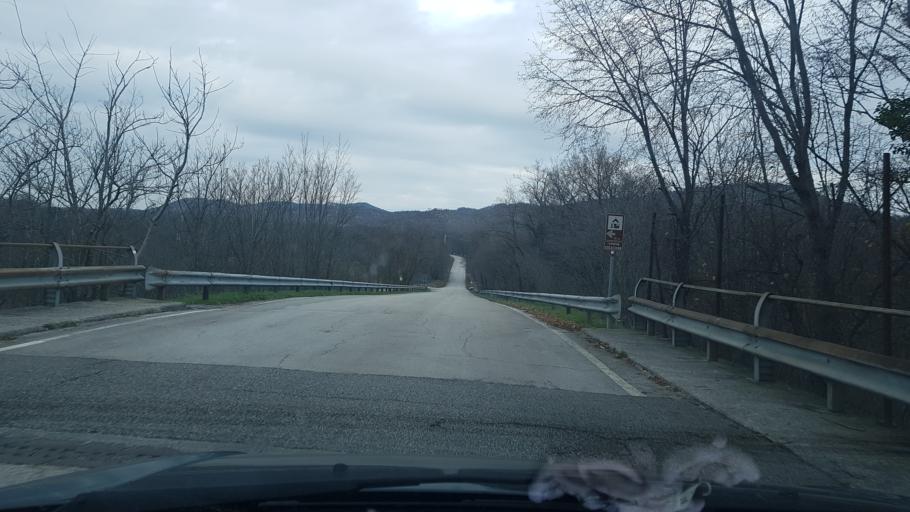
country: IT
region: Friuli Venezia Giulia
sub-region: Provincia di Trieste
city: Zolla
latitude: 45.7011
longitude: 13.8295
